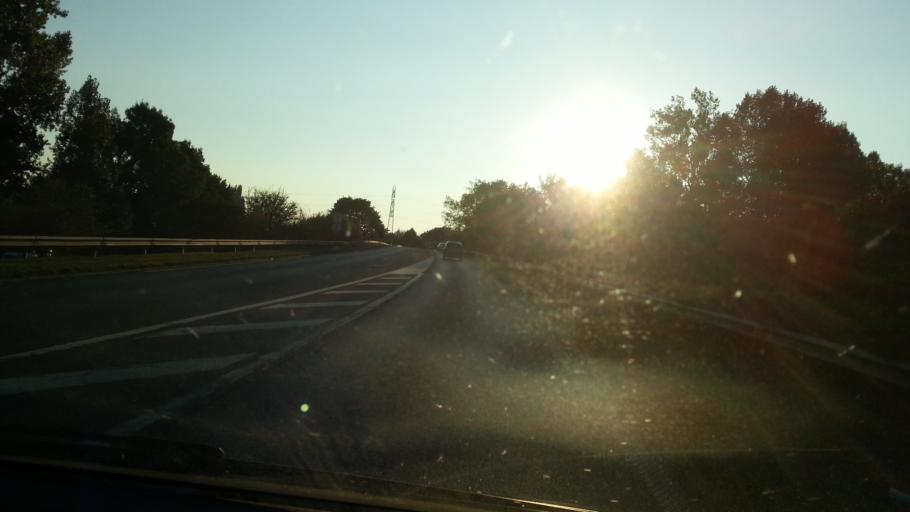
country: FR
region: Picardie
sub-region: Departement de l'Oise
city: Villers-Saint-Paul
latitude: 49.2839
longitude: 2.4805
